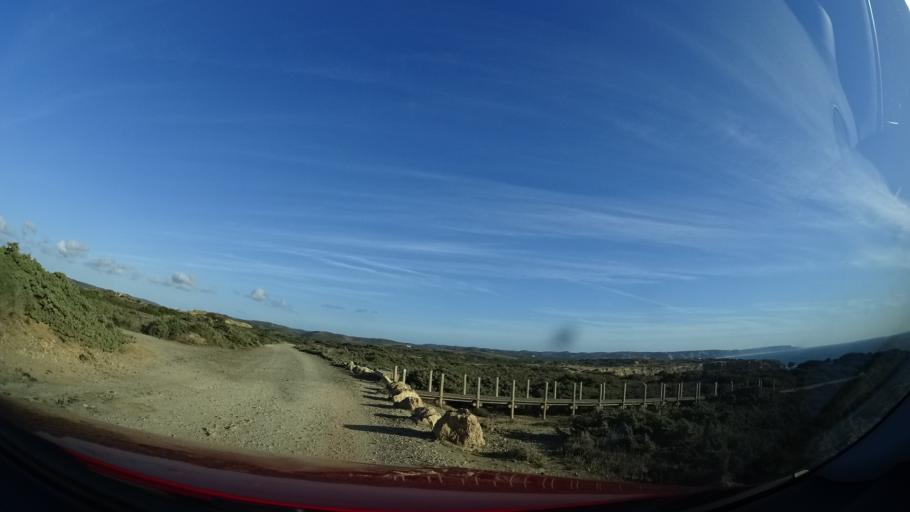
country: PT
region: Faro
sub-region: Vila do Bispo
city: Vila do Bispo
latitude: 37.1913
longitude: -8.9101
